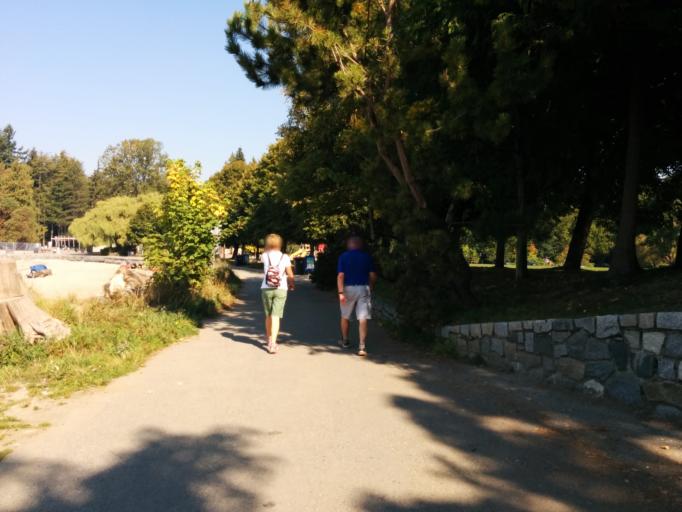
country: CA
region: British Columbia
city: West End
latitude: 49.2940
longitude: -123.1498
